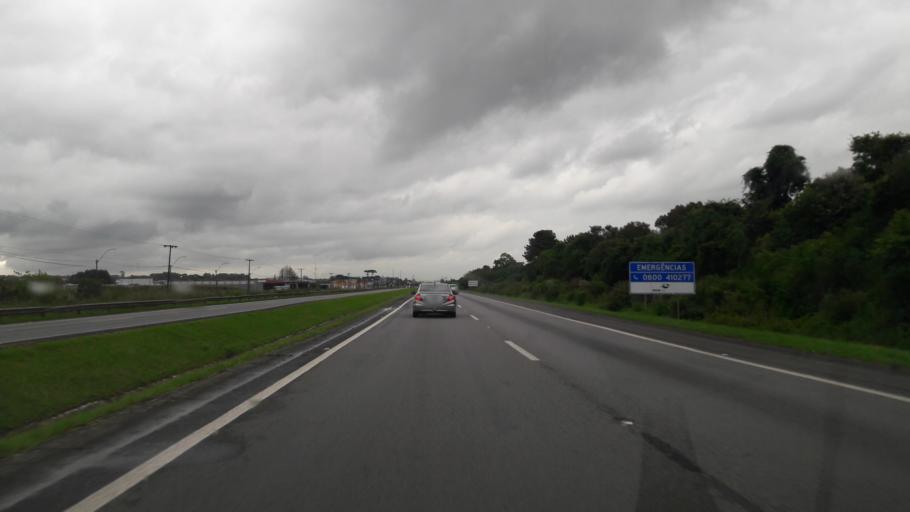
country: BR
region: Parana
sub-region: Piraquara
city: Piraquara
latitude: -25.5347
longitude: -49.0760
